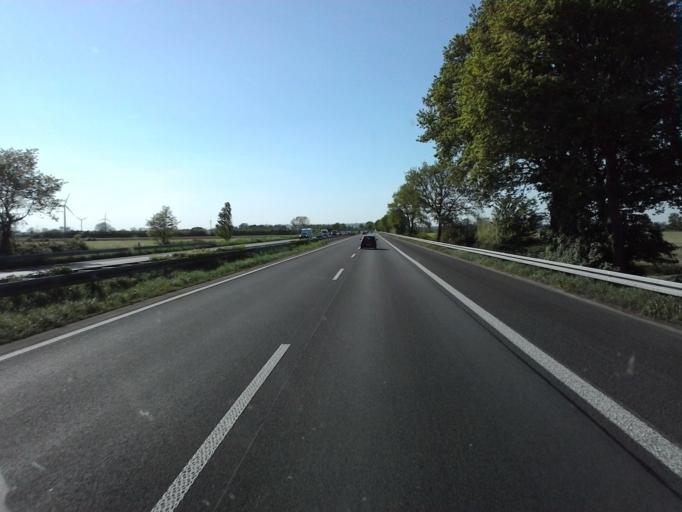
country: NL
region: Gelderland
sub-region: Oude IJsselstreek
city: Gendringen
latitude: 51.8390
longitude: 6.3523
